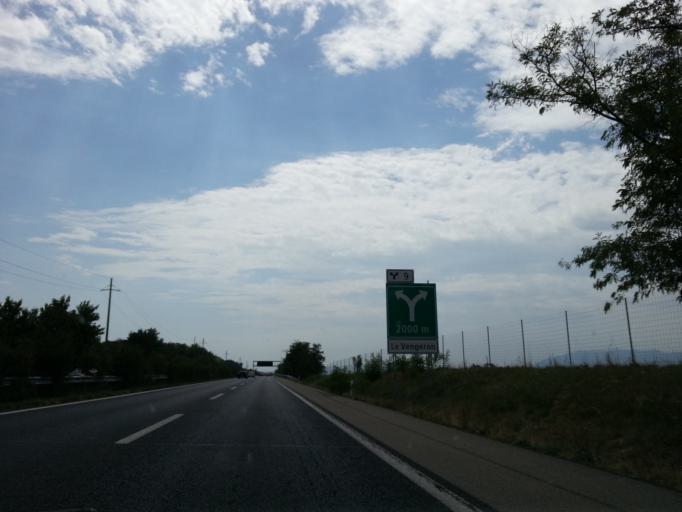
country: CH
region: Geneva
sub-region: Geneva
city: Bellevue
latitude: 46.2733
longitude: 6.1393
